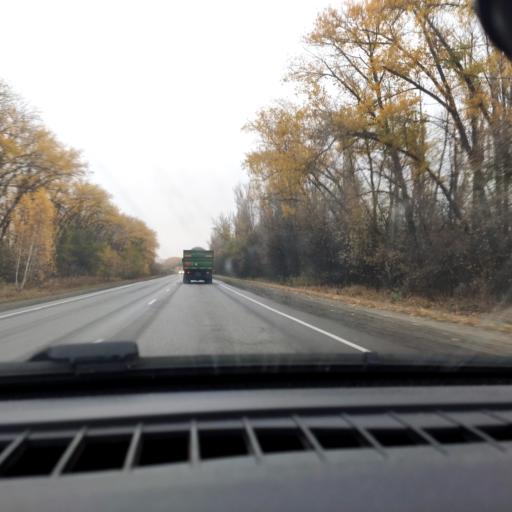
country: RU
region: Voronezj
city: Ostrogozhsk
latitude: 50.9671
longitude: 39.0099
